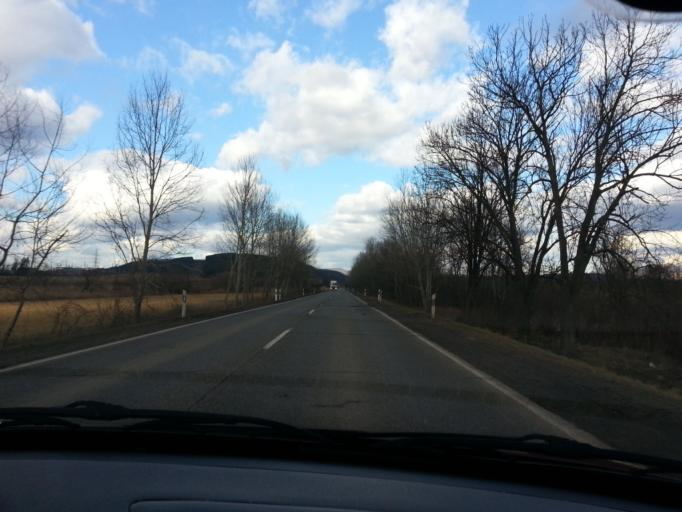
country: HU
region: Nograd
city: Batonyterenye
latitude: 47.9835
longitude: 19.8133
